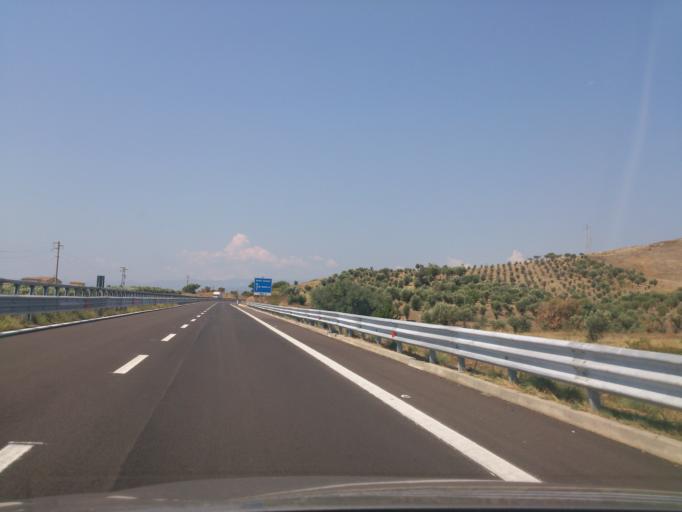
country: IT
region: Calabria
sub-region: Provincia di Reggio Calabria
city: Roccella Ionica
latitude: 38.3126
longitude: 16.3646
